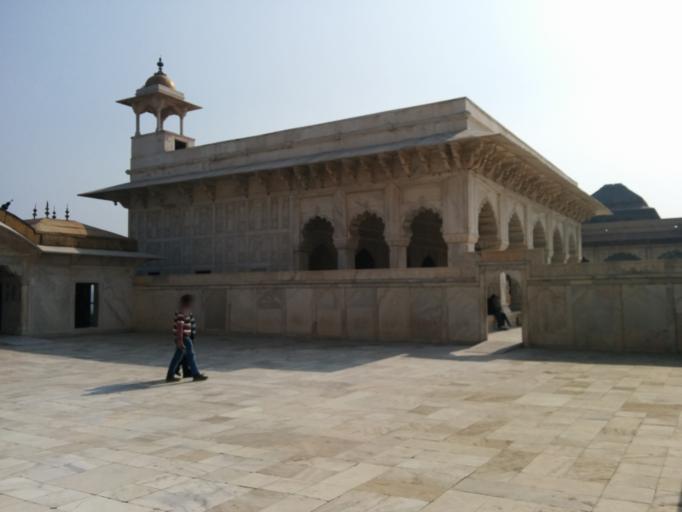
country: IN
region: Uttar Pradesh
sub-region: Agra
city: Agra
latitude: 27.1787
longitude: 78.0235
